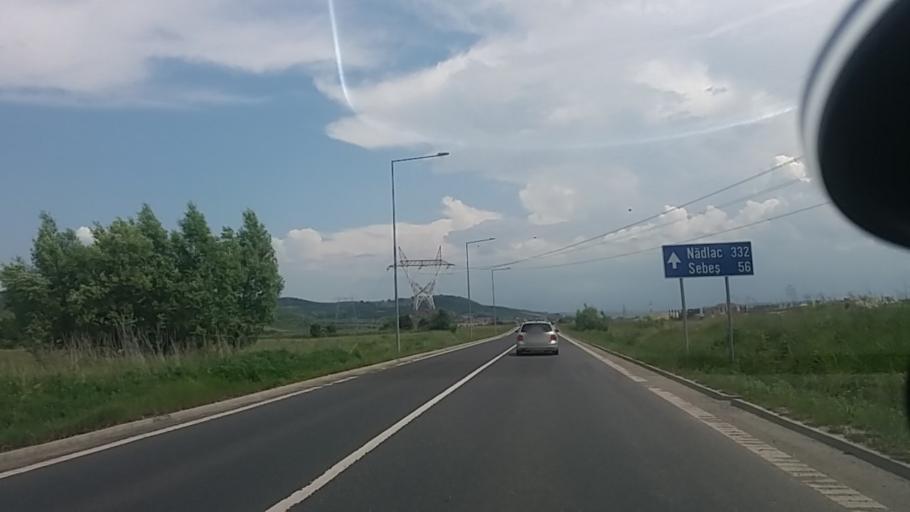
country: RO
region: Sibiu
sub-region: Municipiul Sibiu
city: Sibiu
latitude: 45.8247
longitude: 24.1532
